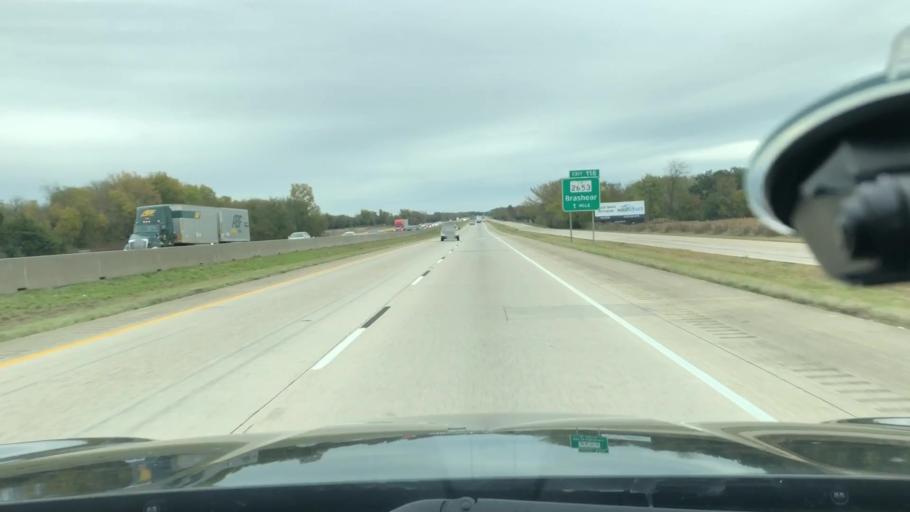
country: US
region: Texas
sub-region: Hopkins County
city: Sulphur Springs
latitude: 33.1292
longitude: -95.7682
